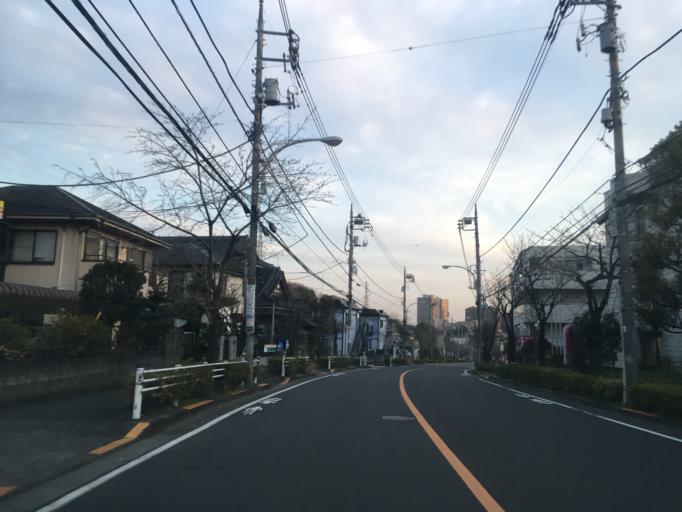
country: JP
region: Tokyo
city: Hino
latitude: 35.6049
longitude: 139.3854
